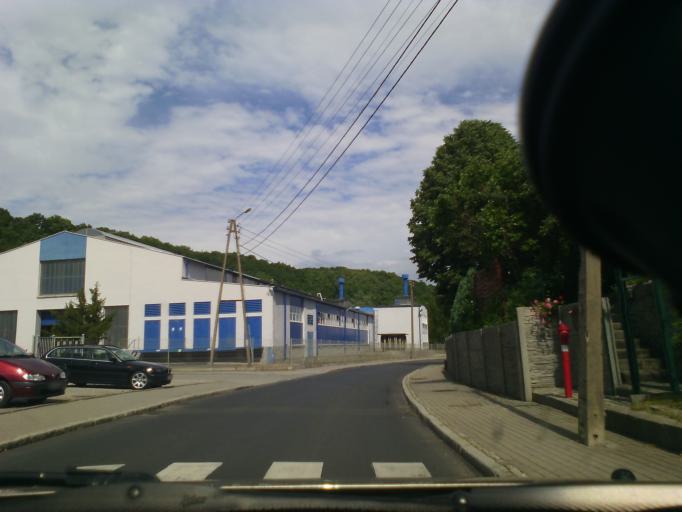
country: PL
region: Lower Silesian Voivodeship
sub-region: Powiat swidnicki
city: Swiebodzice
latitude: 50.8530
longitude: 16.3008
